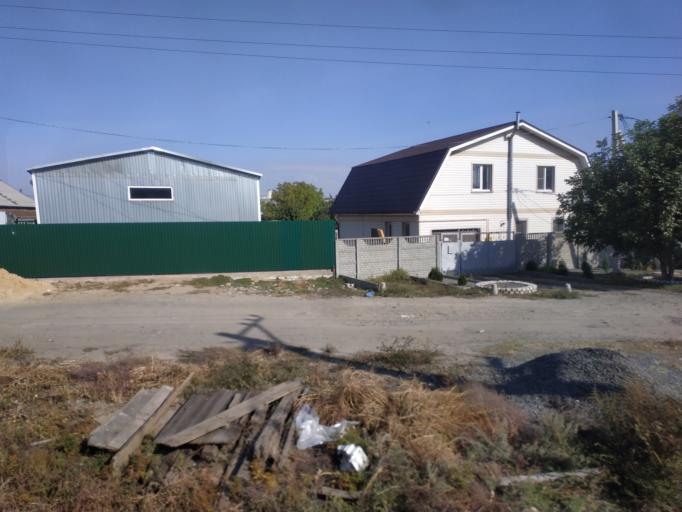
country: RU
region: Volgograd
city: Volgograd
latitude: 48.7499
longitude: 44.5337
